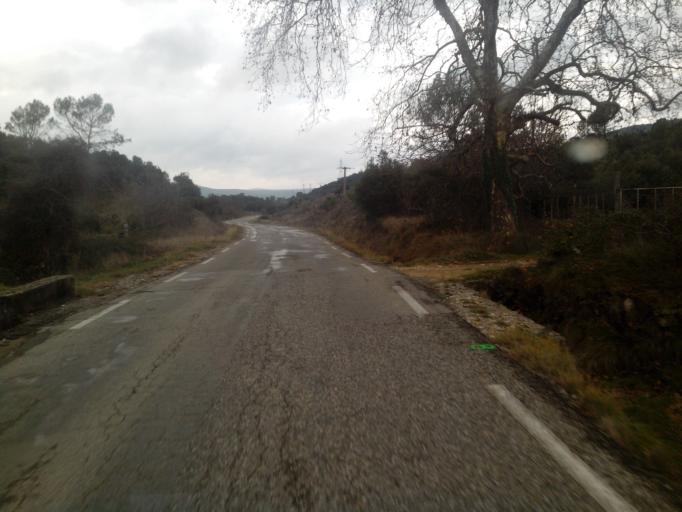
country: FR
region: Languedoc-Roussillon
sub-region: Departement du Gard
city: Saint-Hippolyte-du-Fort
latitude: 43.9481
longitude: 3.8081
